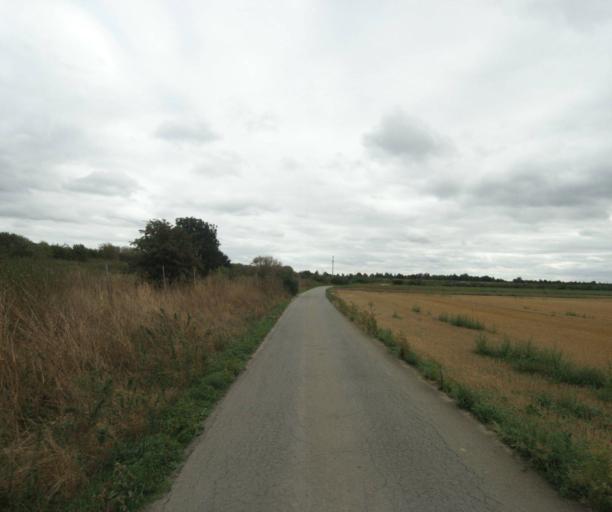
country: FR
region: Nord-Pas-de-Calais
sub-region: Departement du Nord
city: Fretin
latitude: 50.5696
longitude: 3.1357
